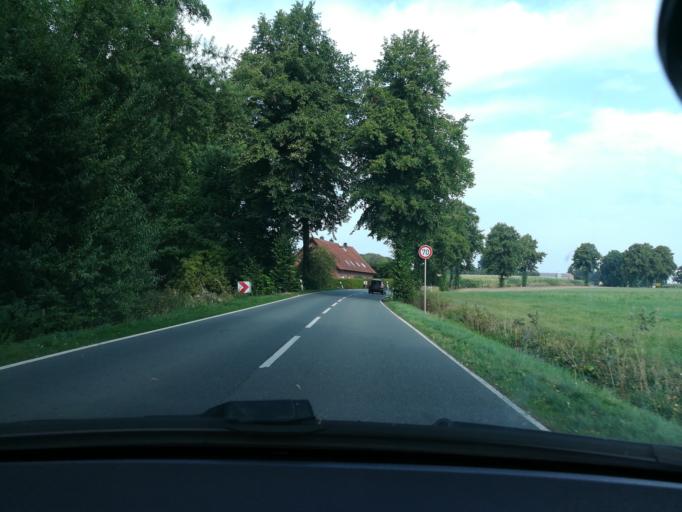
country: DE
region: Lower Saxony
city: Melle
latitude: 52.1590
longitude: 8.3313
